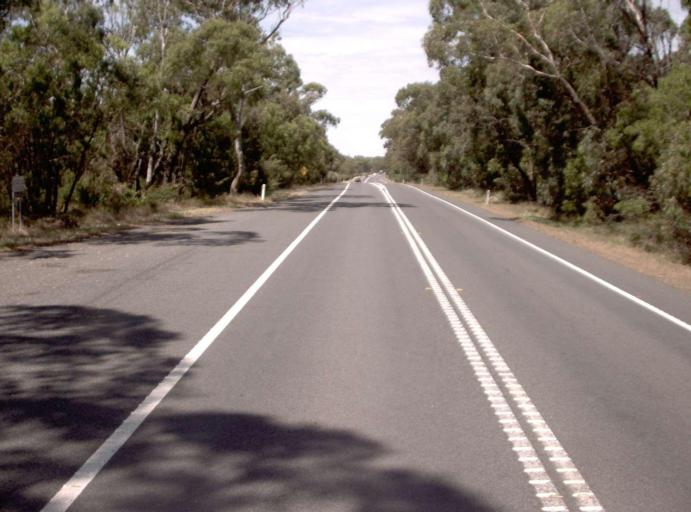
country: AU
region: Victoria
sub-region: Wellington
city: Sale
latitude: -37.9412
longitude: 147.1449
